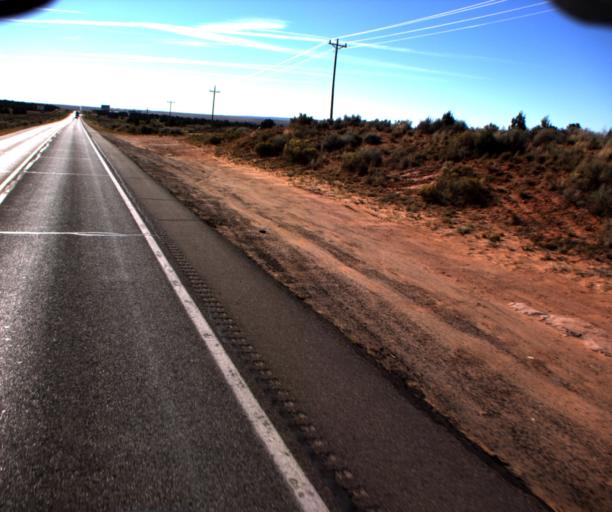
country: US
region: Arizona
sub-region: Mohave County
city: Colorado City
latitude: 36.9679
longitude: -112.9729
